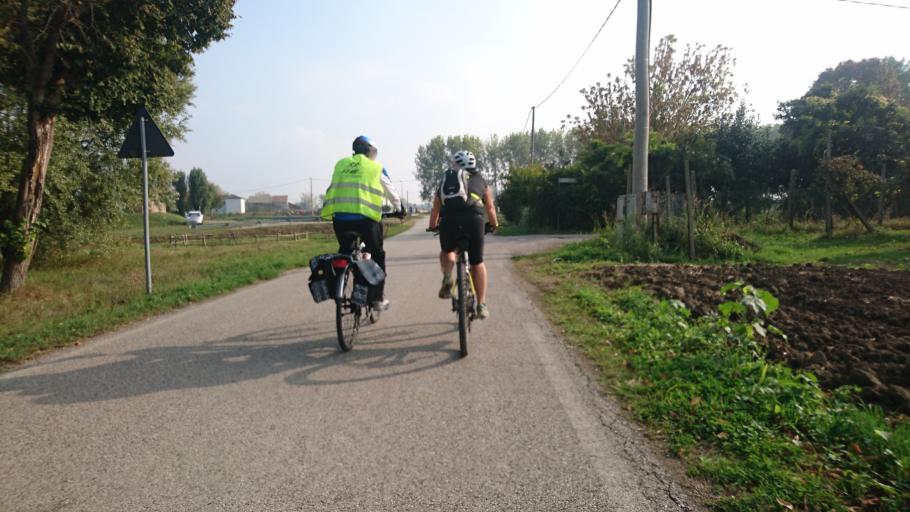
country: IT
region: Veneto
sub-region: Provincia di Rovigo
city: Bosaro
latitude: 44.9938
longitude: 11.7484
